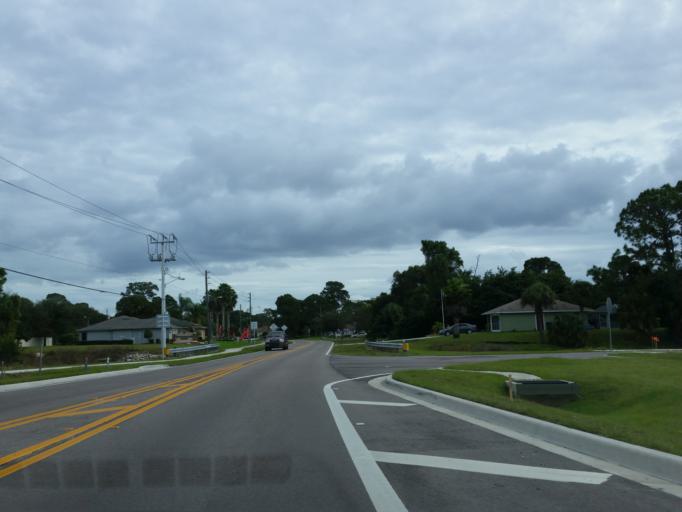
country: US
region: Florida
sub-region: Sarasota County
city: North Port
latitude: 27.0704
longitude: -82.2049
